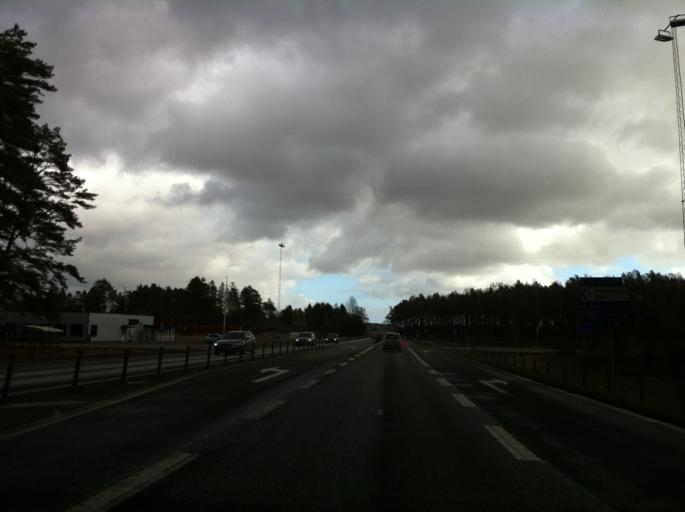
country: SE
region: Skane
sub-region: Kristianstads Kommun
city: Kristianstad
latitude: 56.0169
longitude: 14.1443
